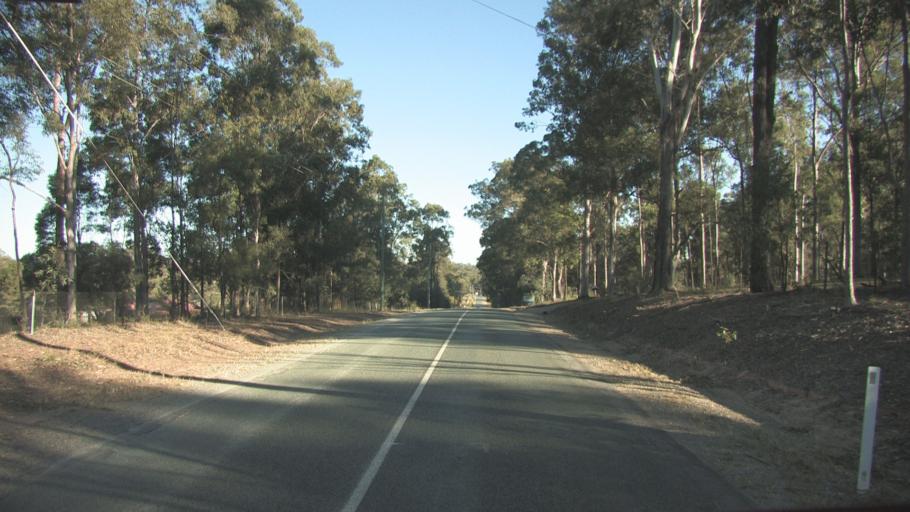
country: AU
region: Queensland
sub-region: Logan
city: Chambers Flat
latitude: -27.7776
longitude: 153.1361
